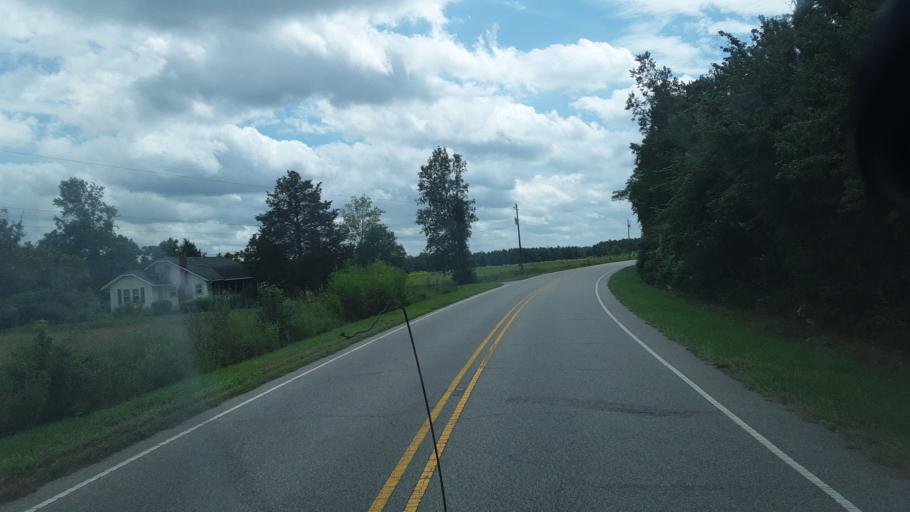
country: US
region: North Carolina
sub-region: Columbus County
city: Tabor City
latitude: 34.2883
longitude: -79.0401
